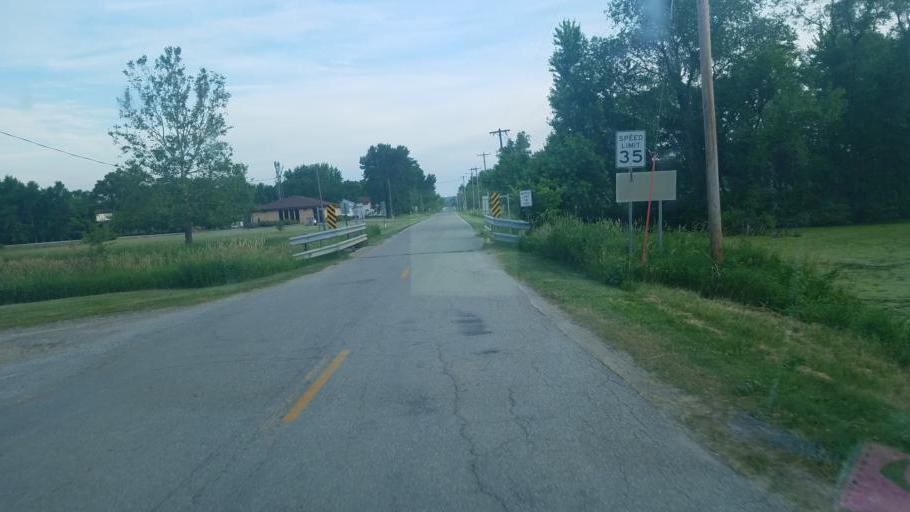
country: US
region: Iowa
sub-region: Benton County
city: Belle Plaine
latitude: 41.9274
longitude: -92.3946
